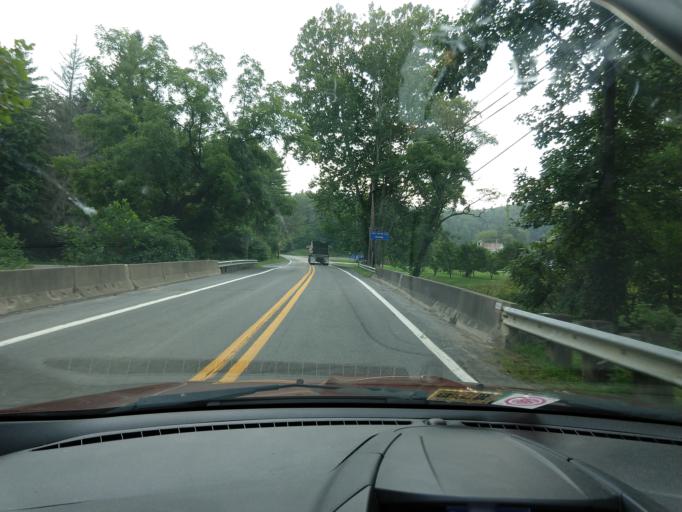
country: US
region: Virginia
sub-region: City of Covington
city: Covington
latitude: 37.9656
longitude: -80.1306
